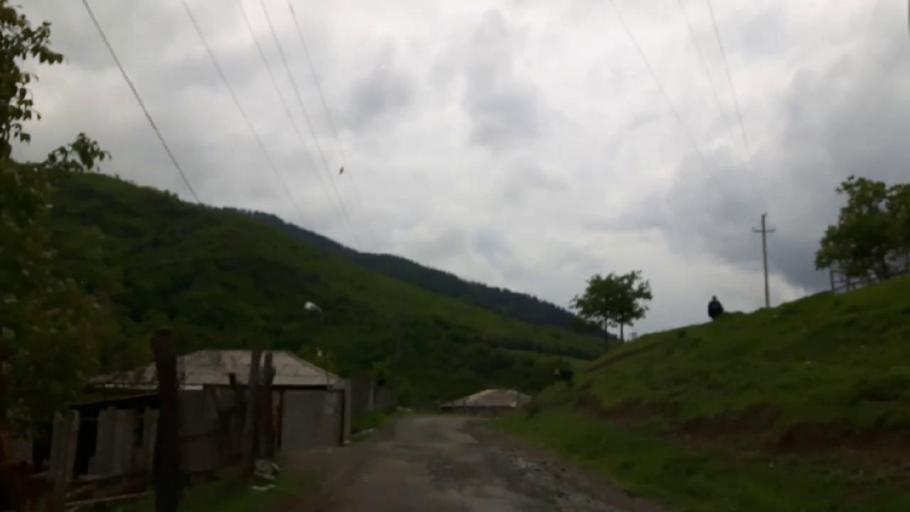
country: GE
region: Shida Kartli
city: Gori
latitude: 41.8896
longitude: 44.0088
